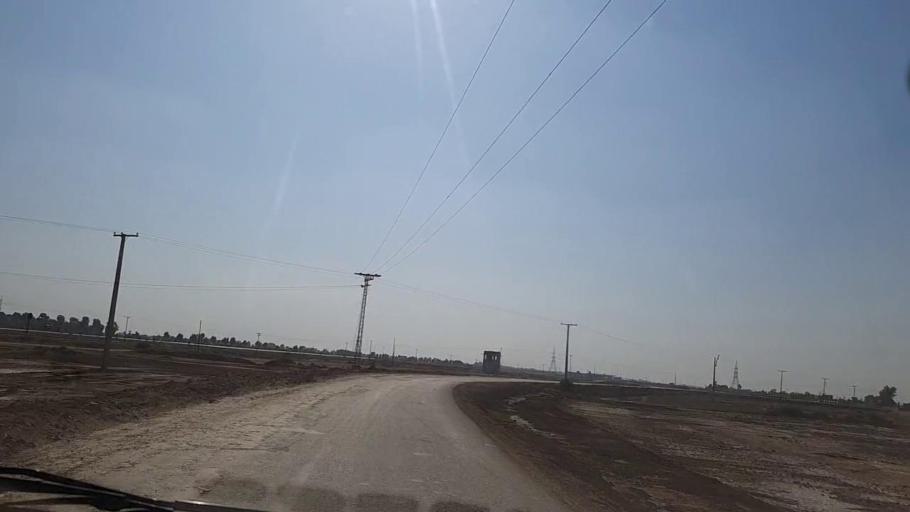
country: PK
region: Sindh
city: Mirpur Khas
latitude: 25.5169
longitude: 68.9522
